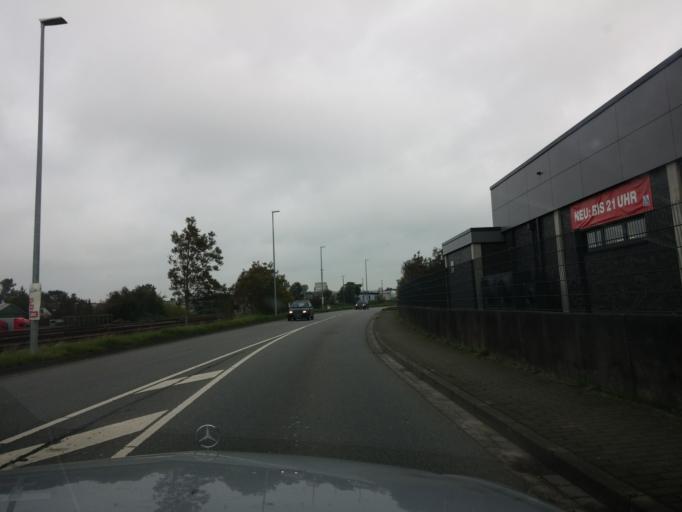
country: DE
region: Schleswig-Holstein
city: Husum
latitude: 54.4825
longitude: 9.0394
